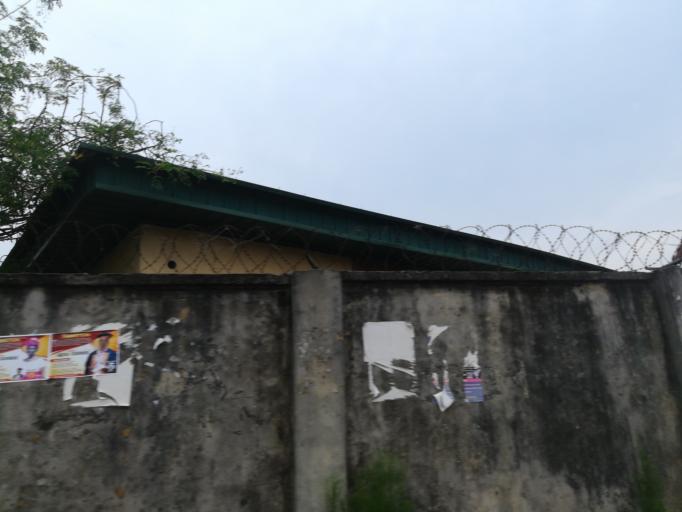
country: NG
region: Rivers
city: Okrika
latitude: 4.7825
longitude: 7.1284
